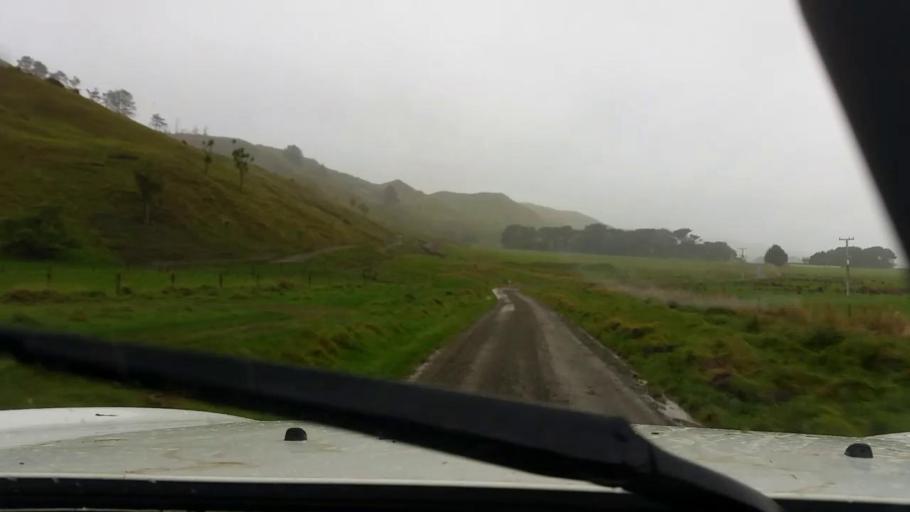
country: NZ
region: Wellington
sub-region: Masterton District
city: Masterton
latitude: -41.2604
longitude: 175.8972
